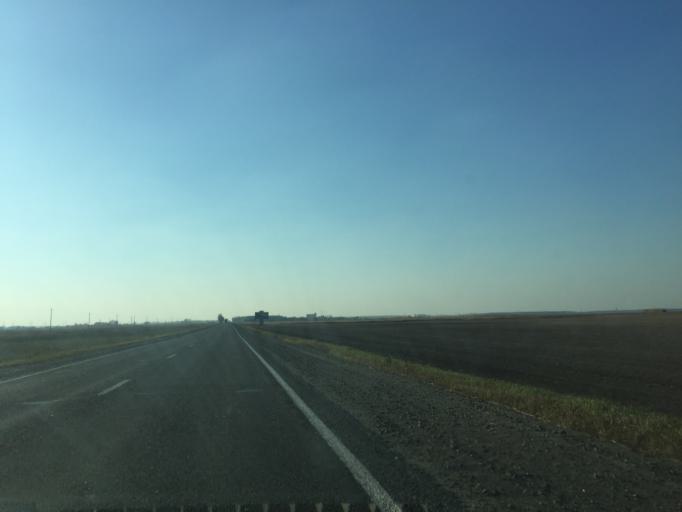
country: BY
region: Gomel
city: Dobrush
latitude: 52.3856
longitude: 31.4129
